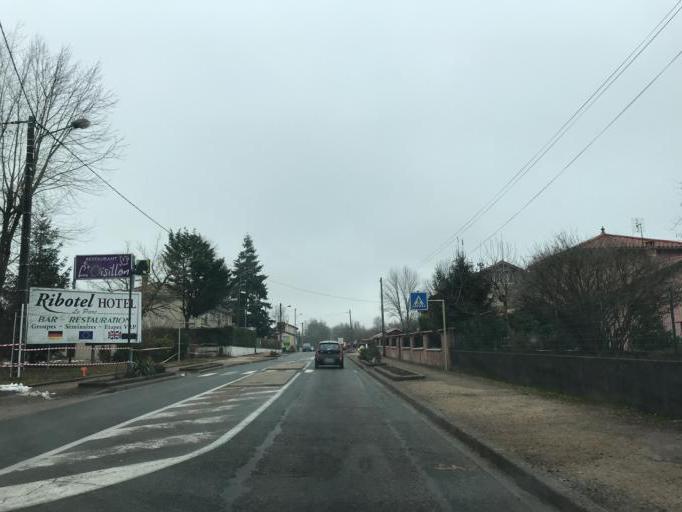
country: FR
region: Rhone-Alpes
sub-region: Departement de l'Ain
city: Villars-les-Dombes
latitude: 45.9975
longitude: 5.0284
